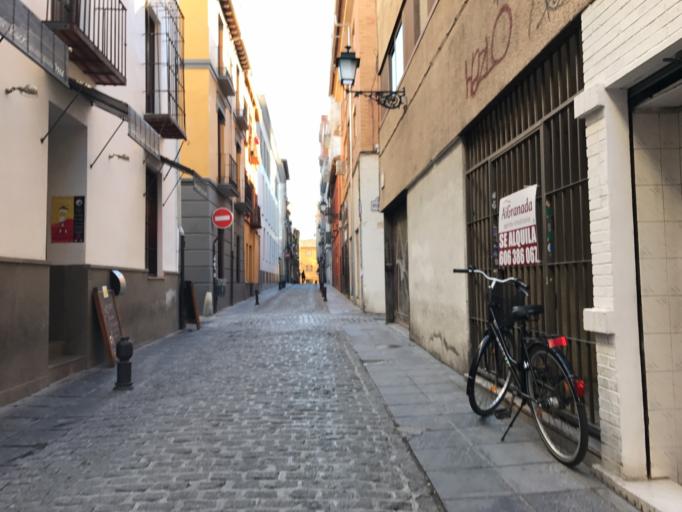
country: ES
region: Andalusia
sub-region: Provincia de Granada
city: Granada
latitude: 37.1772
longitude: -3.6040
